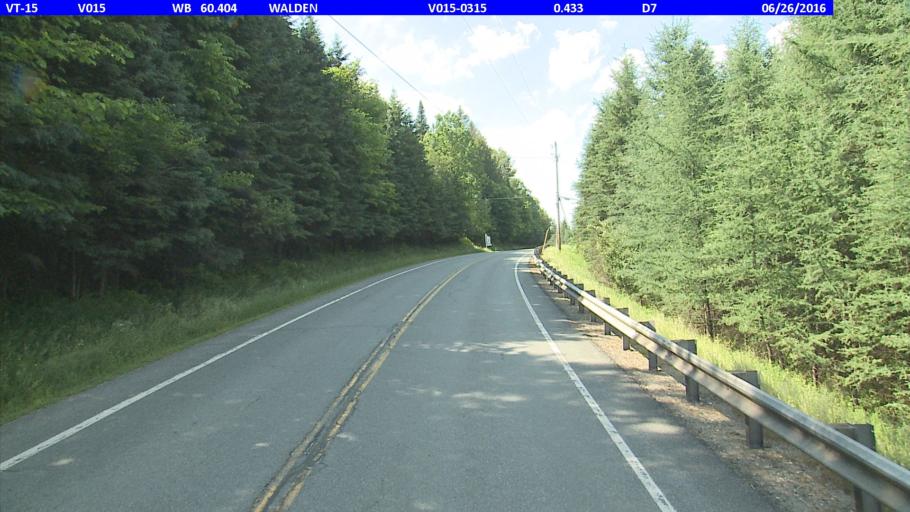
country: US
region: Vermont
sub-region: Caledonia County
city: Hardwick
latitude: 44.4789
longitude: -72.3015
